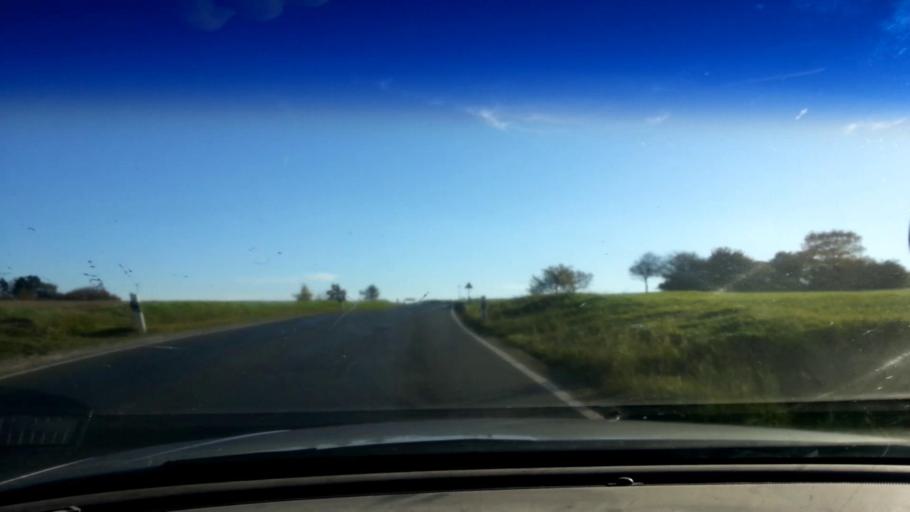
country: DE
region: Bavaria
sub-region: Upper Franconia
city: Poxdorf
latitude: 49.8975
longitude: 11.0934
